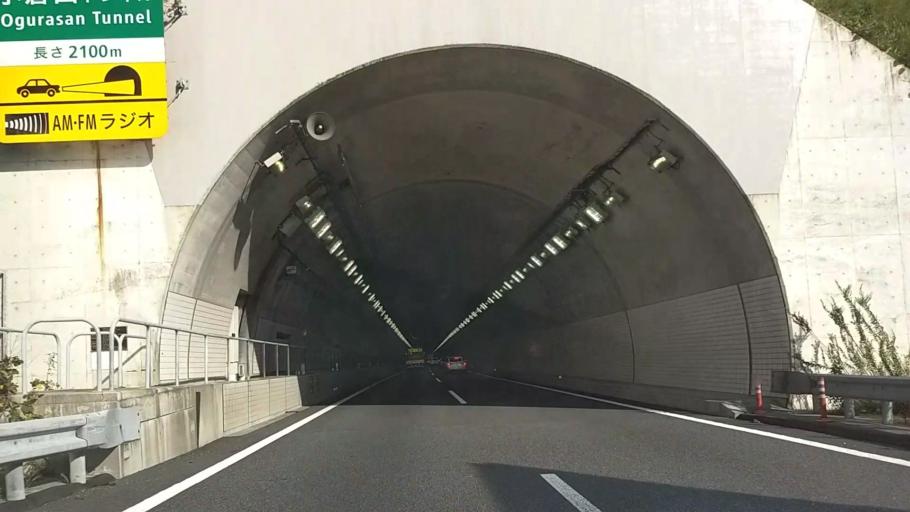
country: JP
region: Tokyo
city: Hachioji
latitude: 35.5598
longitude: 139.3121
